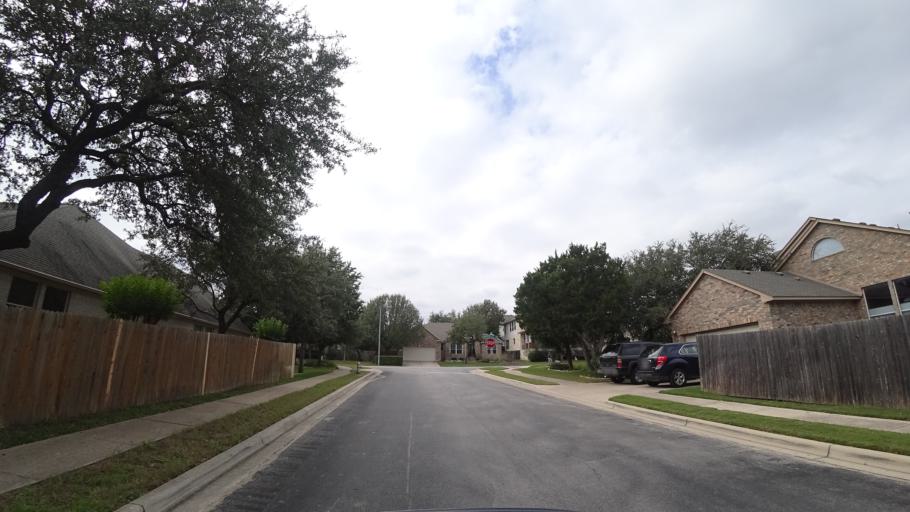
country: US
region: Texas
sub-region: Travis County
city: Shady Hollow
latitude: 30.2167
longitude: -97.8843
